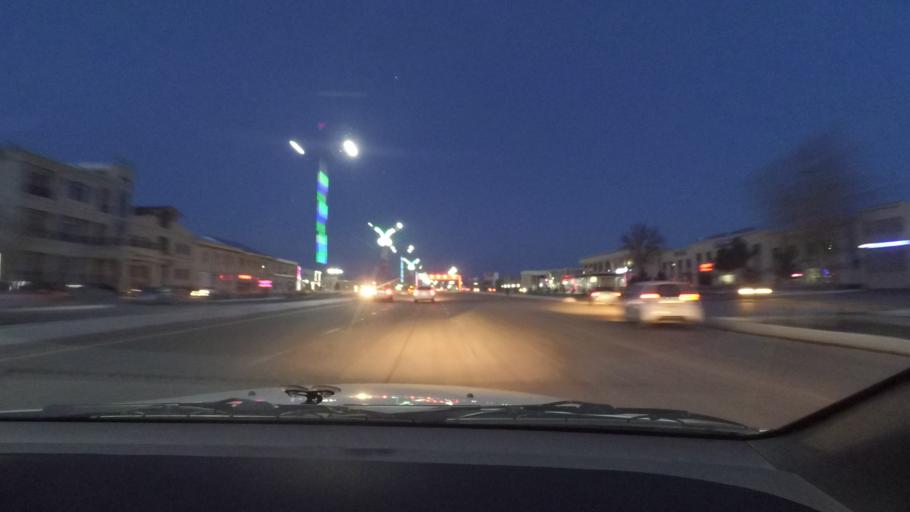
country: UZ
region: Bukhara
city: Bukhara
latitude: 39.7836
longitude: 64.4181
